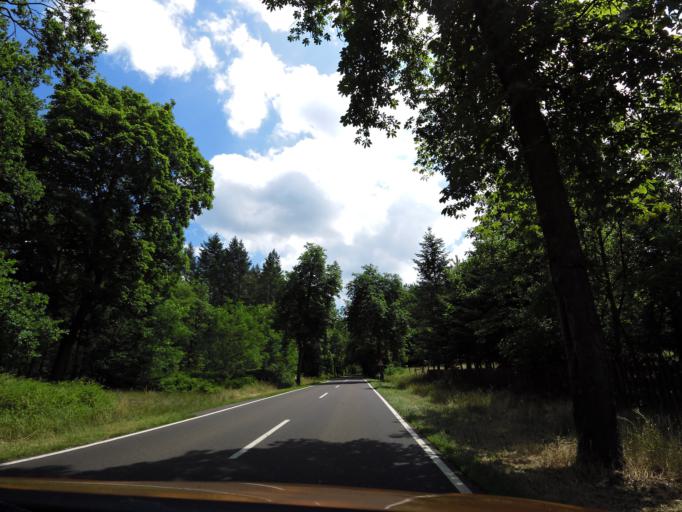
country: DE
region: Brandenburg
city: Nauen
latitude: 52.6279
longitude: 12.9385
